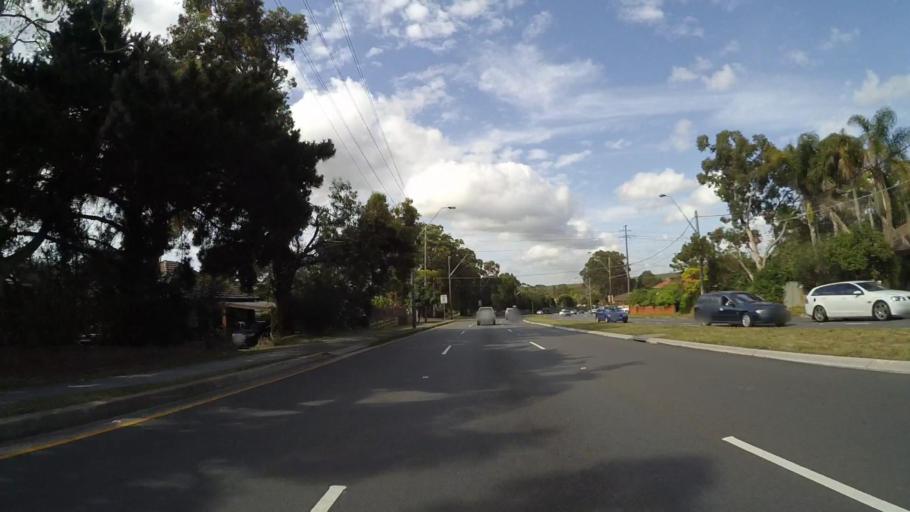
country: AU
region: New South Wales
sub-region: Sutherland Shire
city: Kirrawee
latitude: -34.0363
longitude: 151.0660
